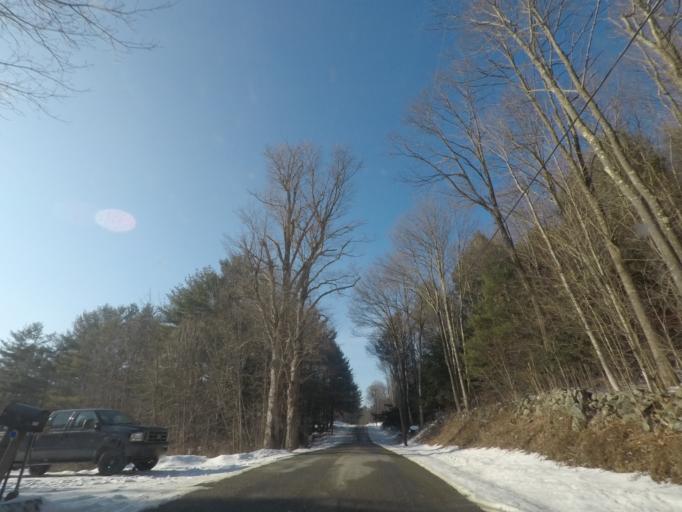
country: US
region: New York
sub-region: Rensselaer County
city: Nassau
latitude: 42.4967
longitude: -73.5002
